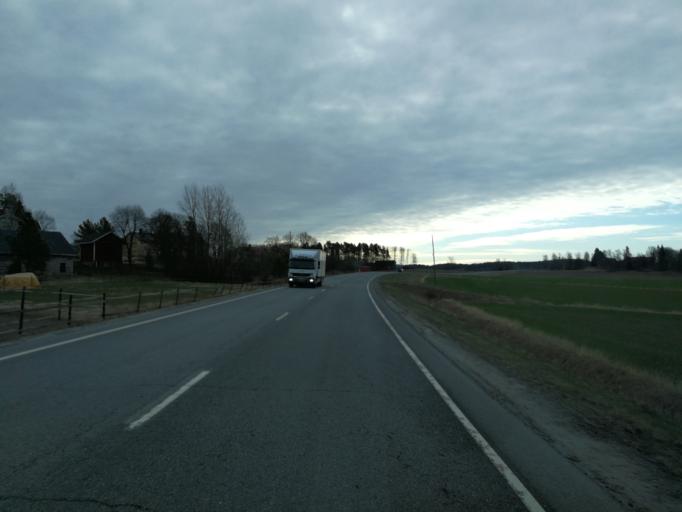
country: FI
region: Varsinais-Suomi
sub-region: Salo
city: Muurla
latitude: 60.3841
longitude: 23.2831
